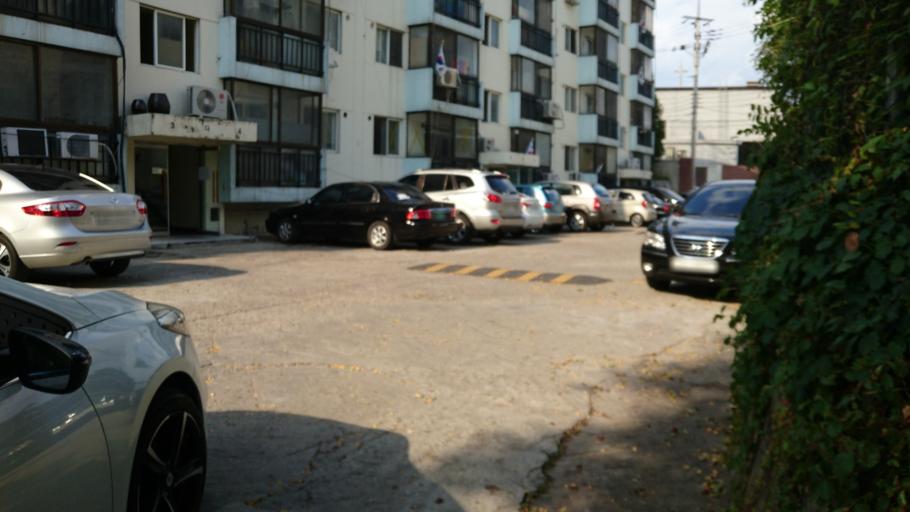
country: KR
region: Seoul
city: Seoul
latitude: 37.5432
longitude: 126.9830
